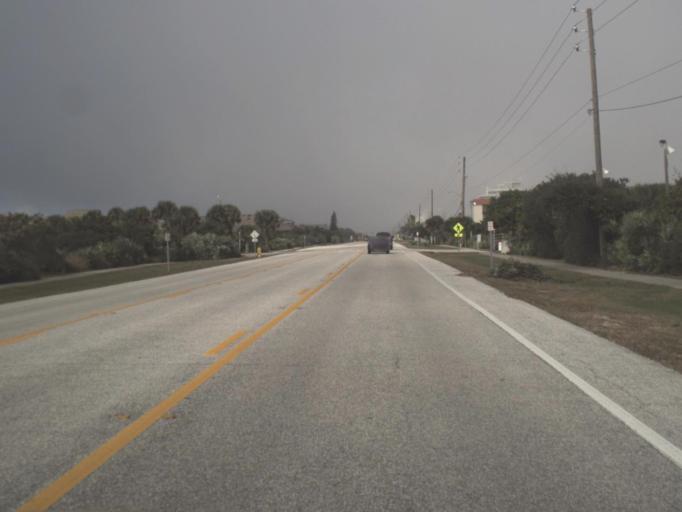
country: US
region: Florida
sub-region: Volusia County
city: Edgewater
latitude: 28.9953
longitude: -80.8707
